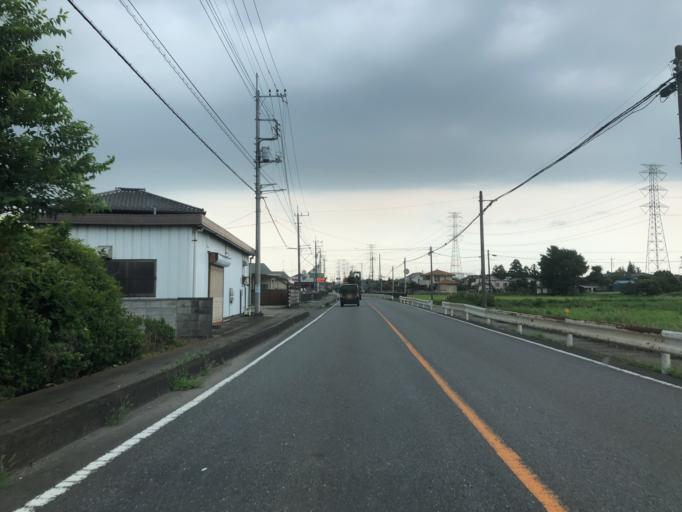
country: JP
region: Saitama
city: Sakado
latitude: 36.0216
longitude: 139.3976
